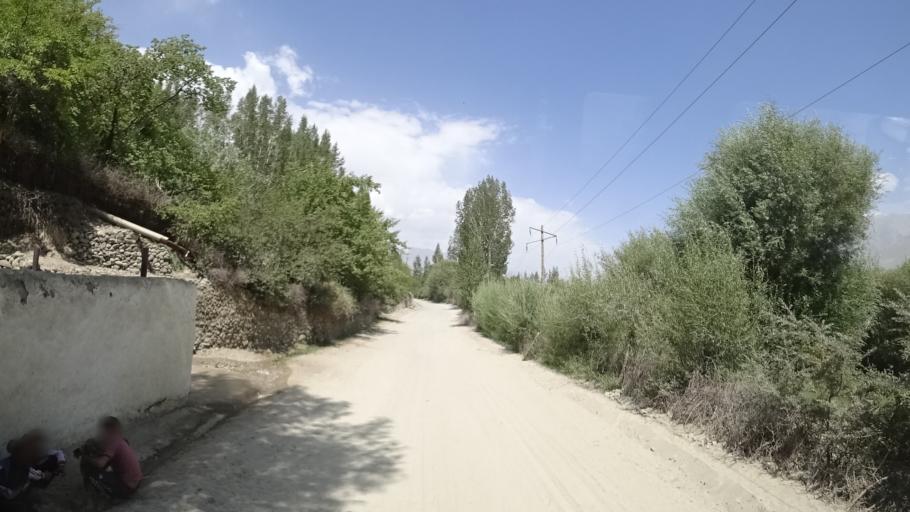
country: AF
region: Badakhshan
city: Khandud
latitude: 36.9411
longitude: 72.2247
